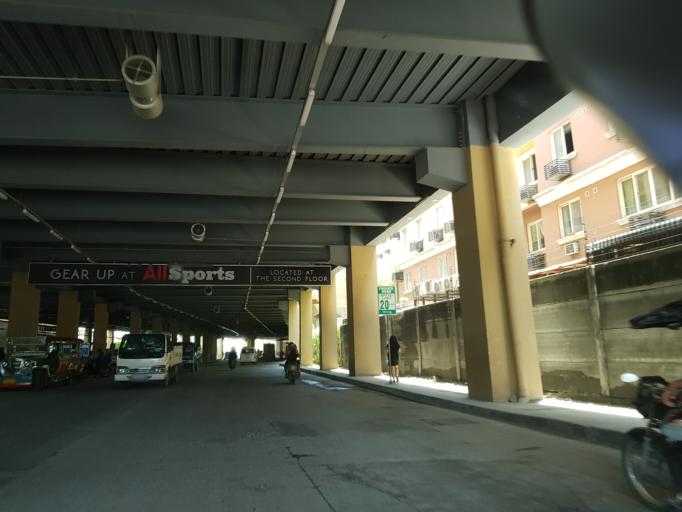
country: PH
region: Calabarzon
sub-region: Province of Rizal
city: Pateros
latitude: 14.5314
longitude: 121.0728
